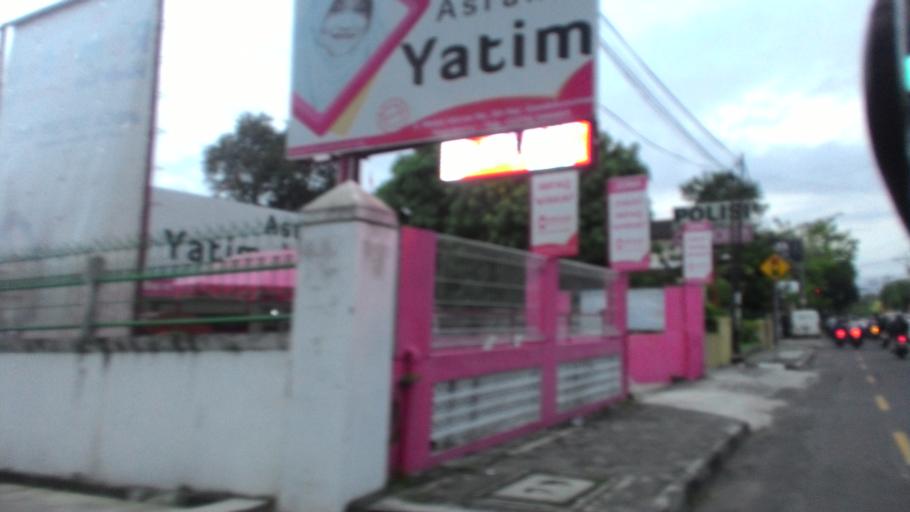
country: ID
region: Daerah Istimewa Yogyakarta
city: Yogyakarta
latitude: -7.7916
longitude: 110.3870
